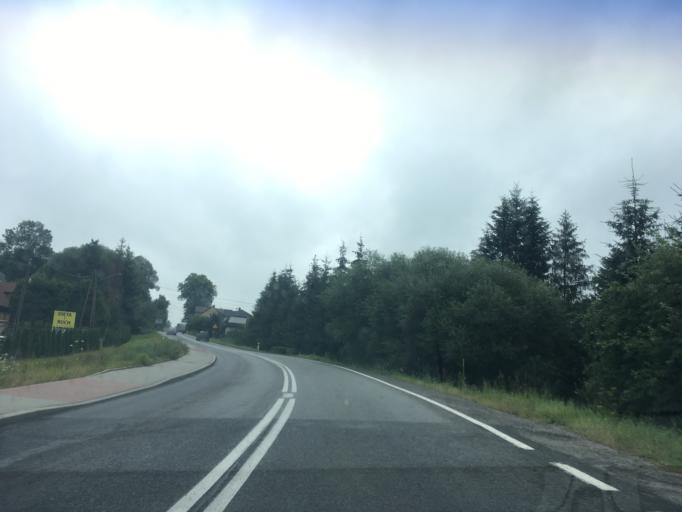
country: PL
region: Lesser Poland Voivodeship
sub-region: Powiat nowotarski
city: Rabka-Zdroj
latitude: 49.6229
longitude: 19.9728
